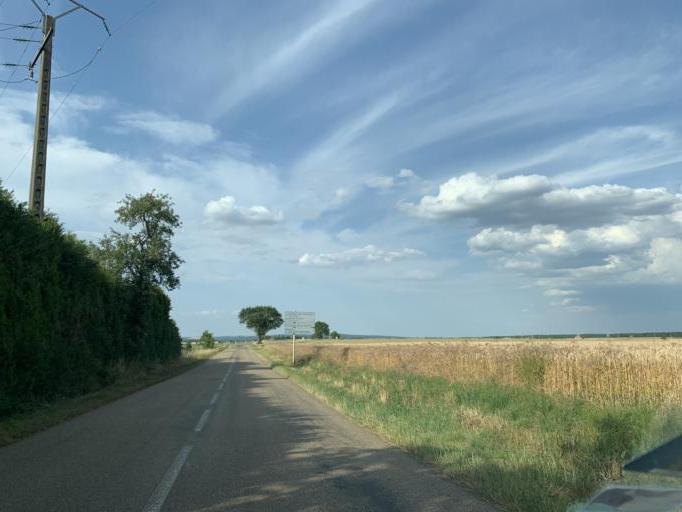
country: FR
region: Bourgogne
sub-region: Departement de l'Yonne
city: Fontenailles
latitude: 47.5047
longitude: 3.3504
